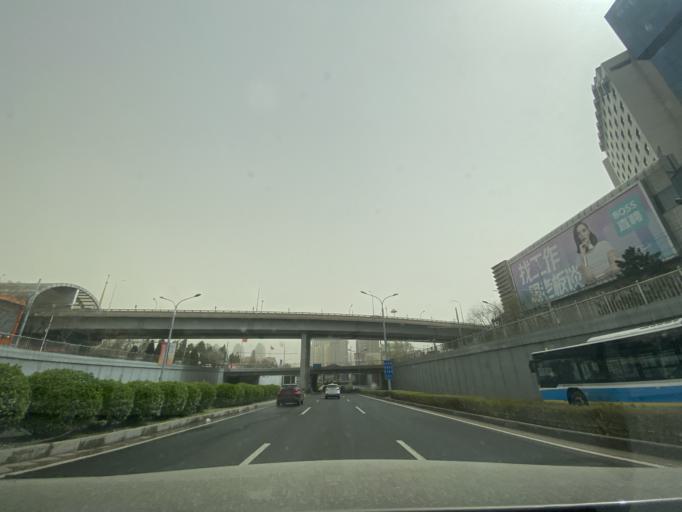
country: CN
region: Beijing
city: Jinrongjie
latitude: 39.9371
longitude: 116.3347
